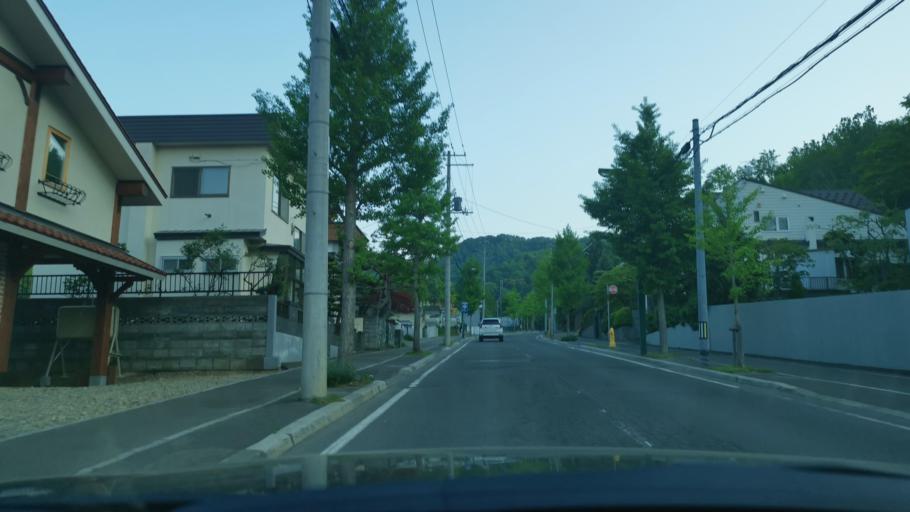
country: JP
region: Hokkaido
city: Sapporo
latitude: 43.0406
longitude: 141.3179
